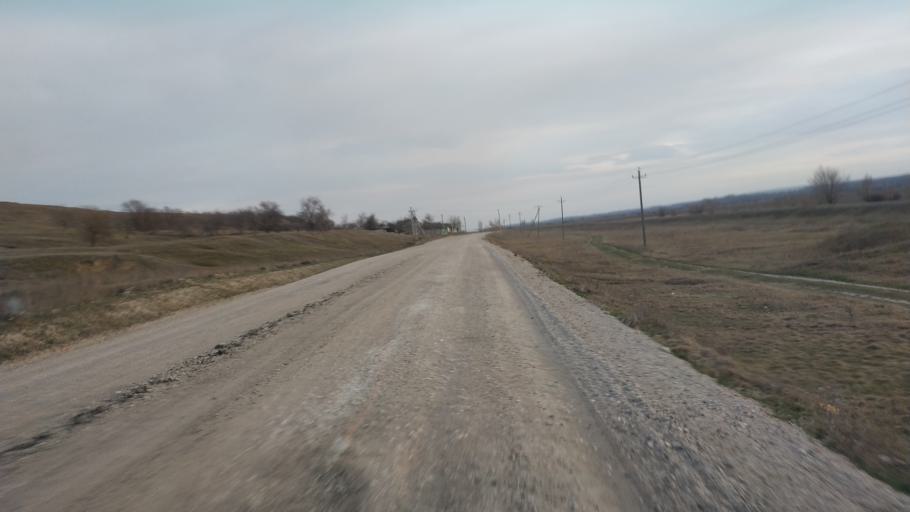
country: MD
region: Hincesti
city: Dancu
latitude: 46.7787
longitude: 28.1968
